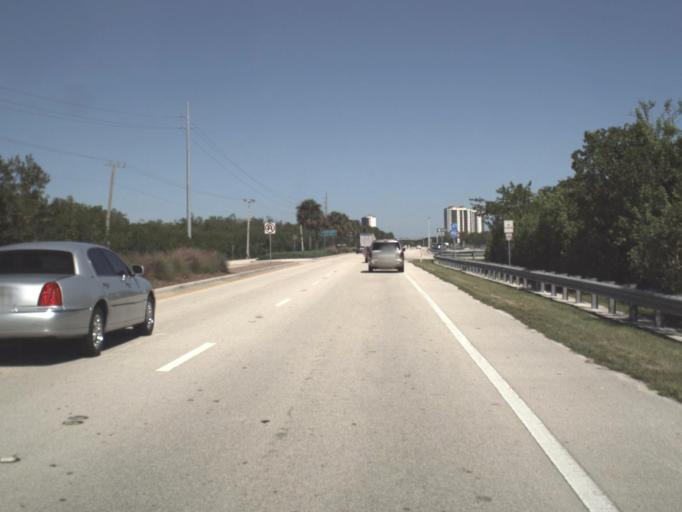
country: US
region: Florida
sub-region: Collier County
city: Marco
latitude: 25.9774
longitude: -81.7047
